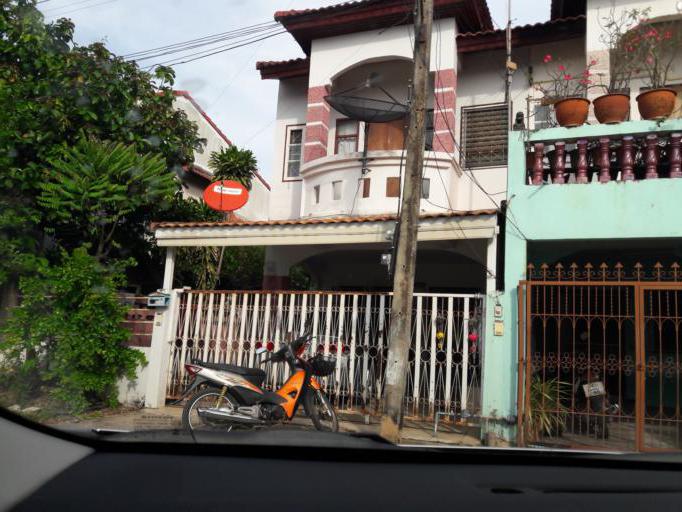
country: TH
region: Ang Thong
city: Ang Thong
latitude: 14.5854
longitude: 100.4451
